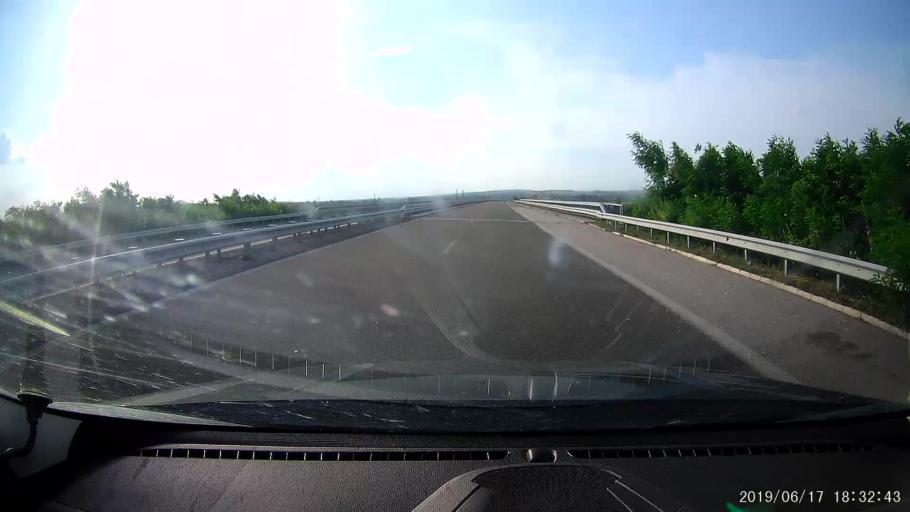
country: BG
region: Khaskovo
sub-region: Obshtina Dimitrovgrad
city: Dimitrovgrad
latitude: 42.0647
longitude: 25.4725
